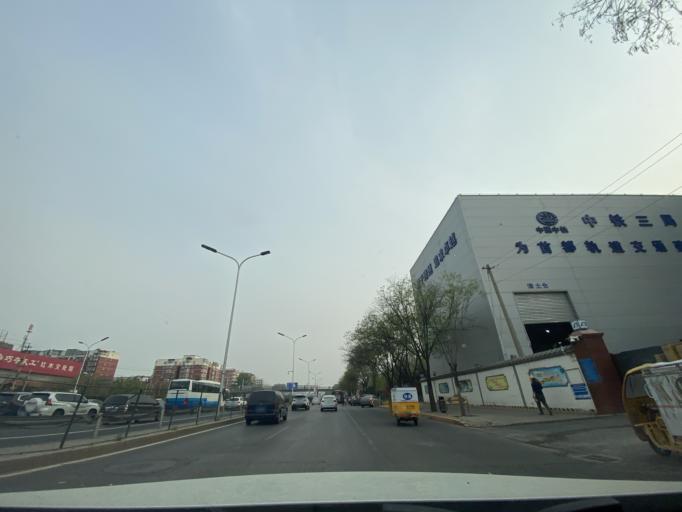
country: CN
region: Beijing
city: Sijiqing
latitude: 39.9368
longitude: 116.2679
